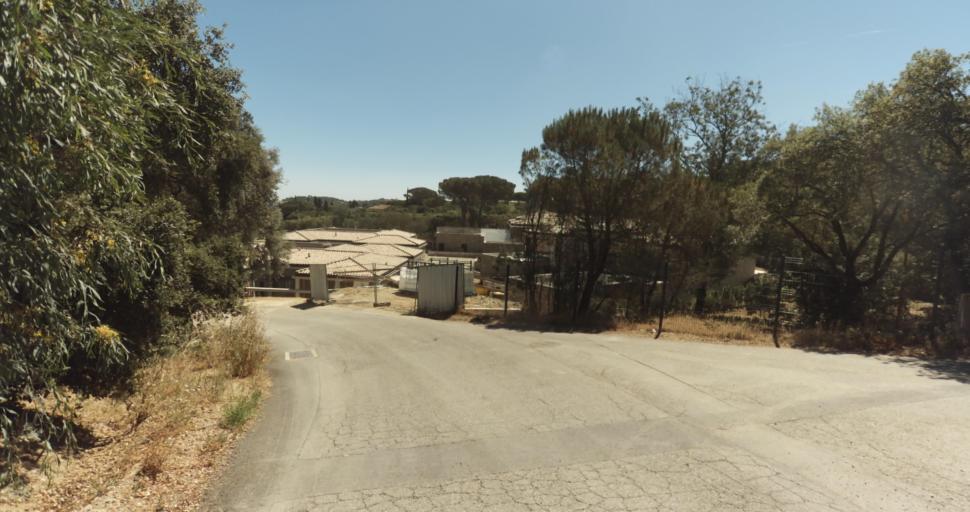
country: FR
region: Provence-Alpes-Cote d'Azur
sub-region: Departement du Var
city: Saint-Tropez
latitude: 43.2625
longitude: 6.6074
